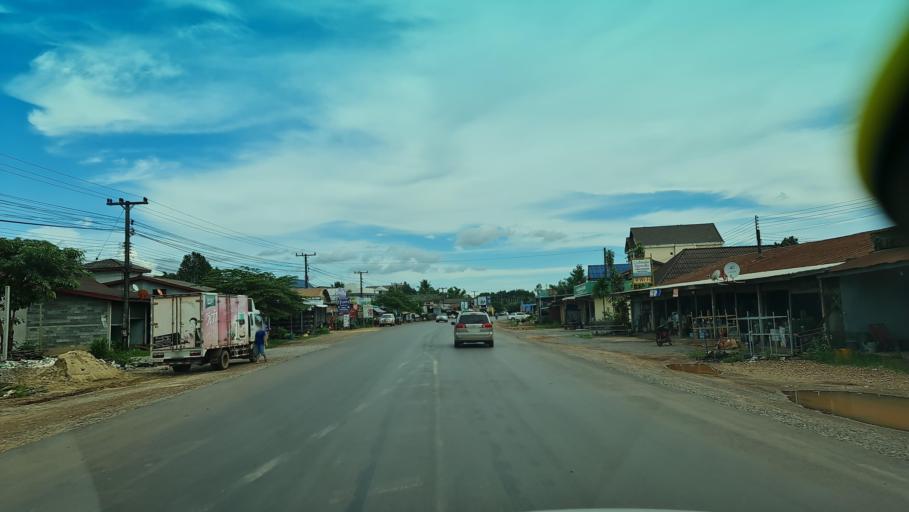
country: TH
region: Nakhon Phanom
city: Ban Phaeng
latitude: 18.1004
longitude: 104.2857
